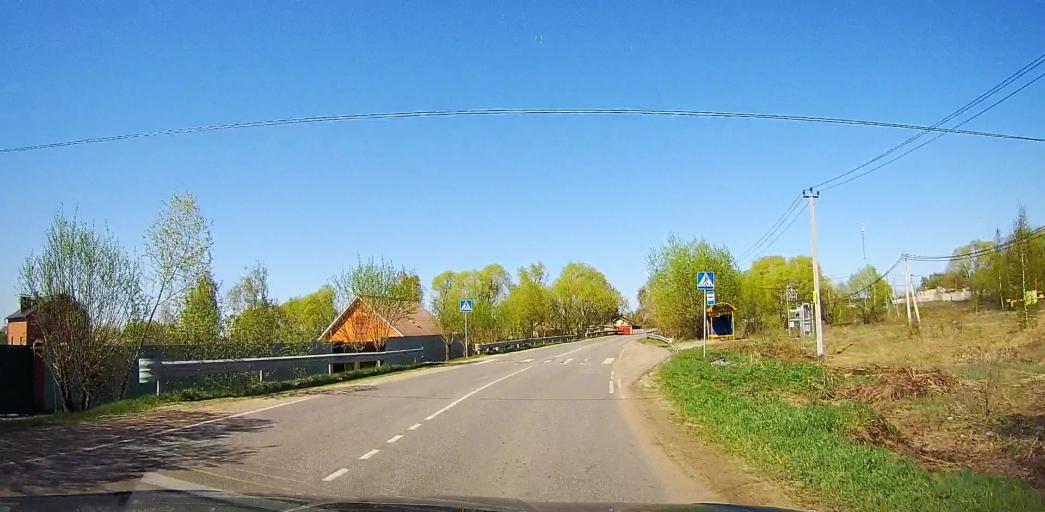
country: RU
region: Moskovskaya
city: Bronnitsy
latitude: 55.4787
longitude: 38.2330
